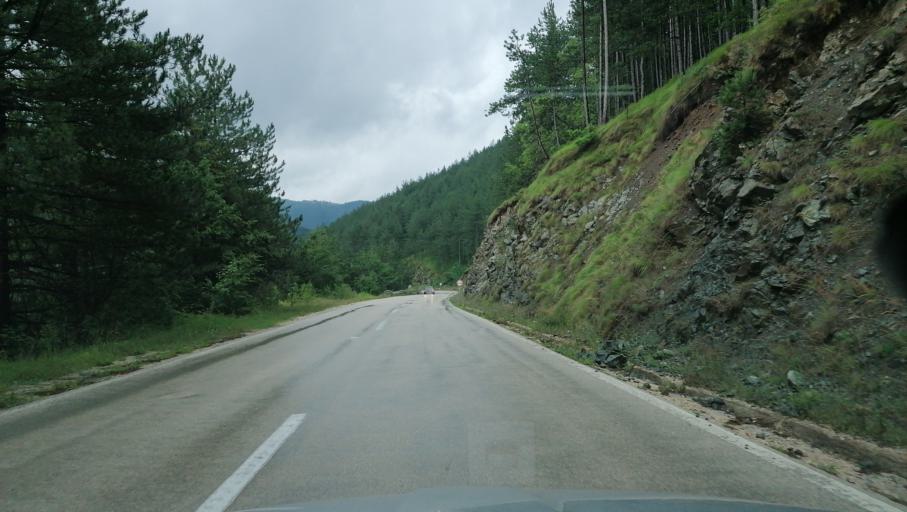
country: RS
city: Durici
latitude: 43.8191
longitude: 19.5072
